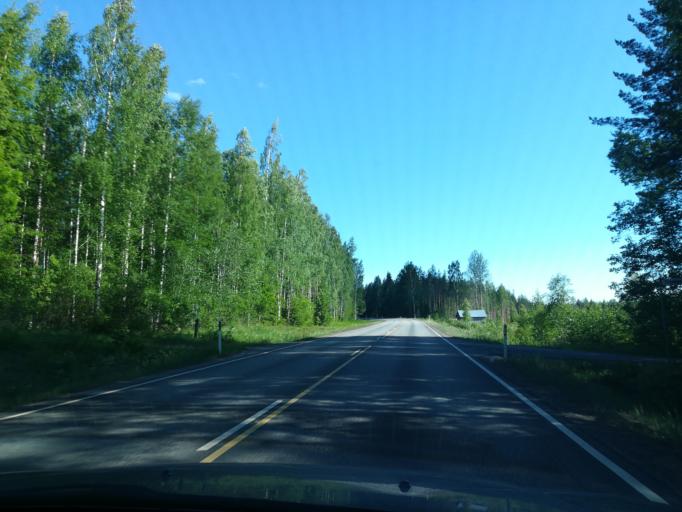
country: FI
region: South Karelia
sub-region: Imatra
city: Ruokolahti
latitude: 61.3781
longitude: 28.6563
